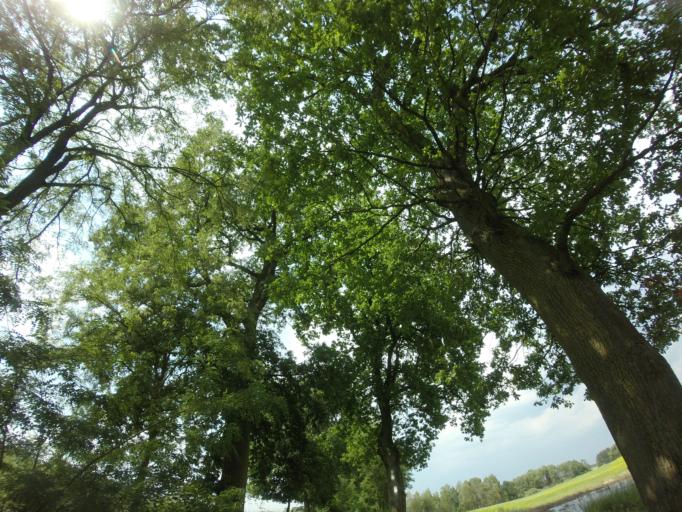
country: PL
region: West Pomeranian Voivodeship
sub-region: Powiat choszczenski
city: Krzecin
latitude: 53.1275
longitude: 15.5911
